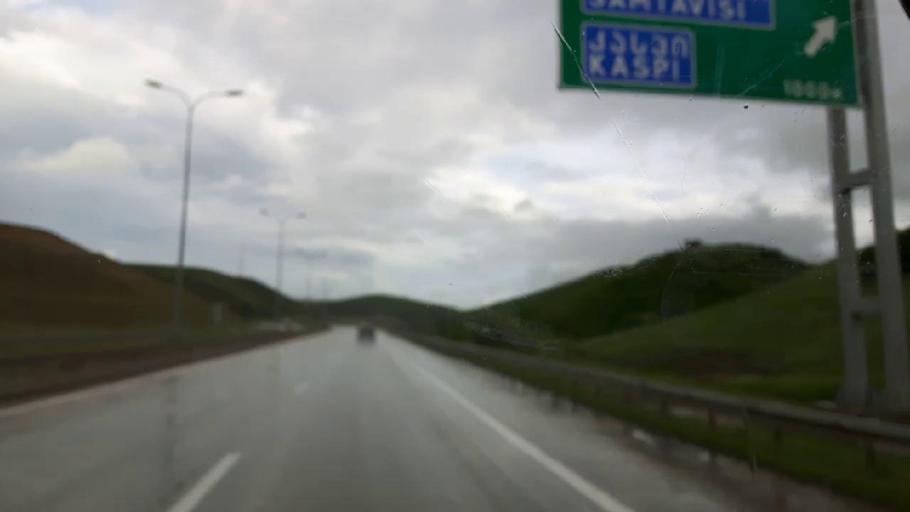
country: GE
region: Shida Kartli
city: Kaspi
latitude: 41.9978
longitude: 44.3985
